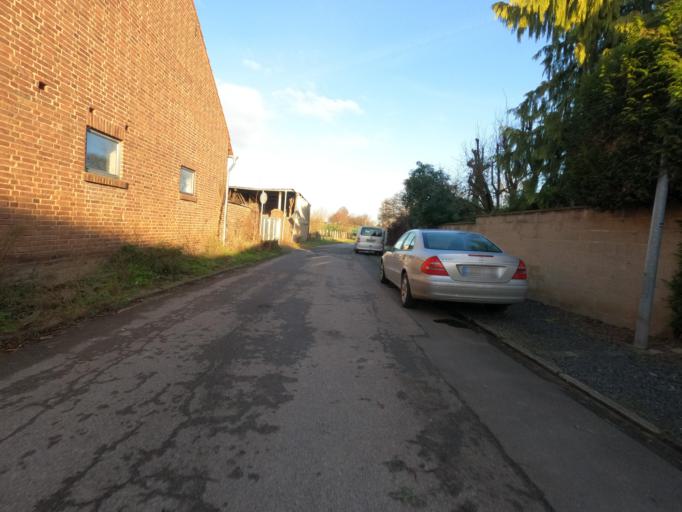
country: DE
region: North Rhine-Westphalia
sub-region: Regierungsbezirk Koln
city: Elsdorf
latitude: 50.9660
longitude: 6.5428
